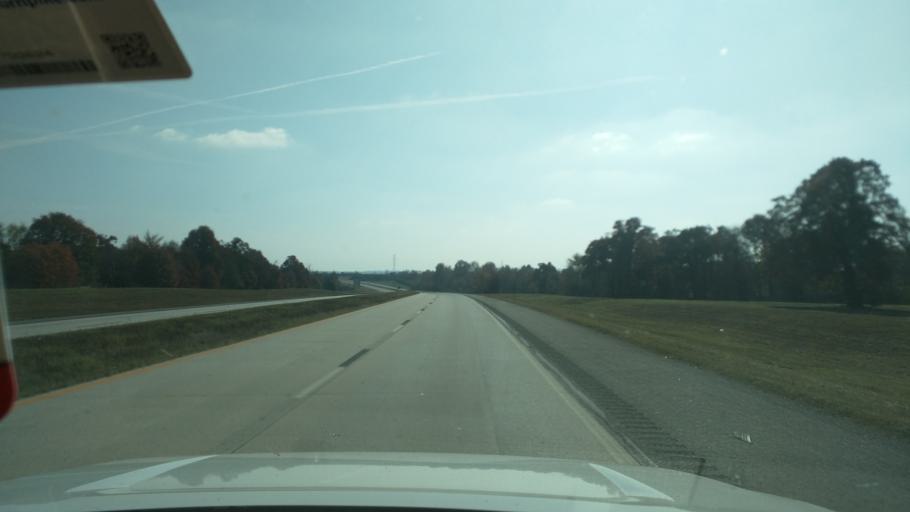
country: US
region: Oklahoma
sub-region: Muskogee County
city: Muskogee
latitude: 35.6462
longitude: -95.3083
